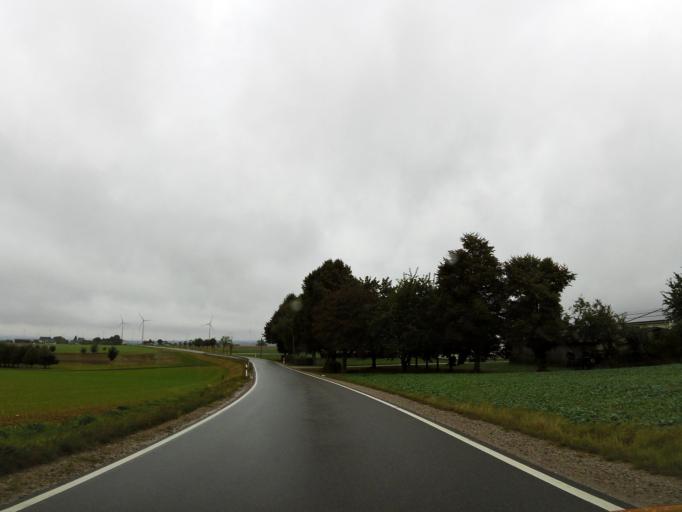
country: DE
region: Rheinland-Pfalz
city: Wahlbach
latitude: 49.9983
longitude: 7.6072
